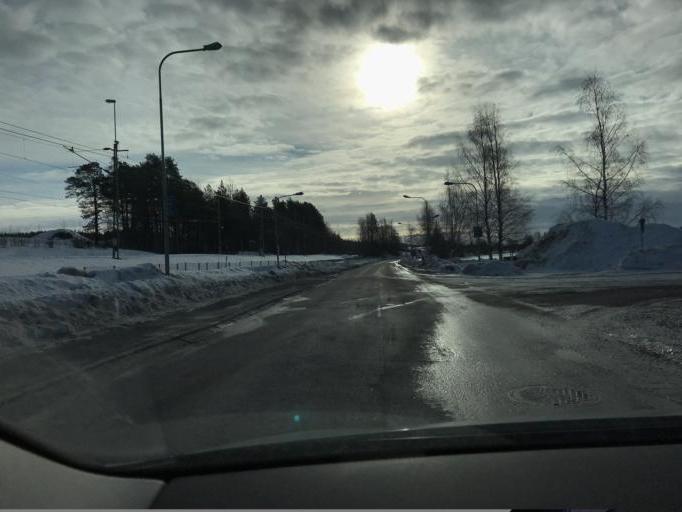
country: SE
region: Norrbotten
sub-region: Lulea Kommun
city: Bergnaset
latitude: 65.6085
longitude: 22.1248
